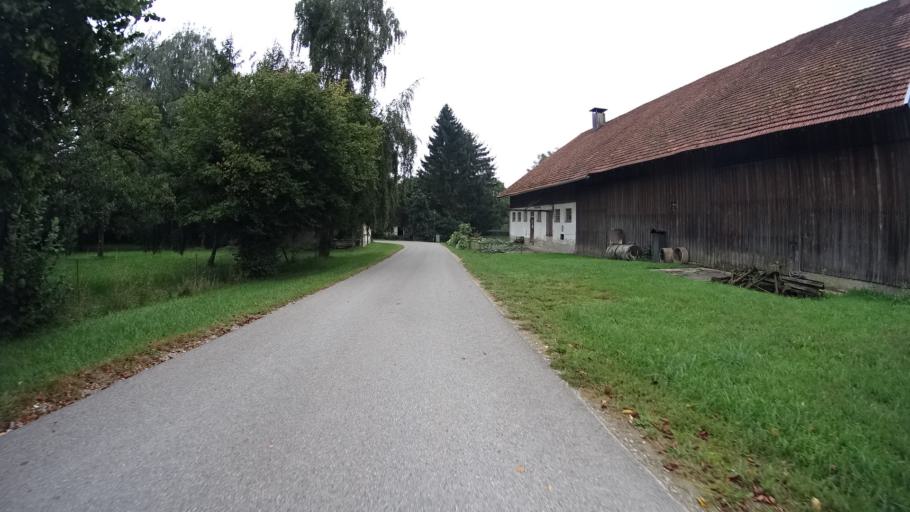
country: DE
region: Bavaria
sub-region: Upper Bavaria
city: Hepberg
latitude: 48.8303
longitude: 11.4882
